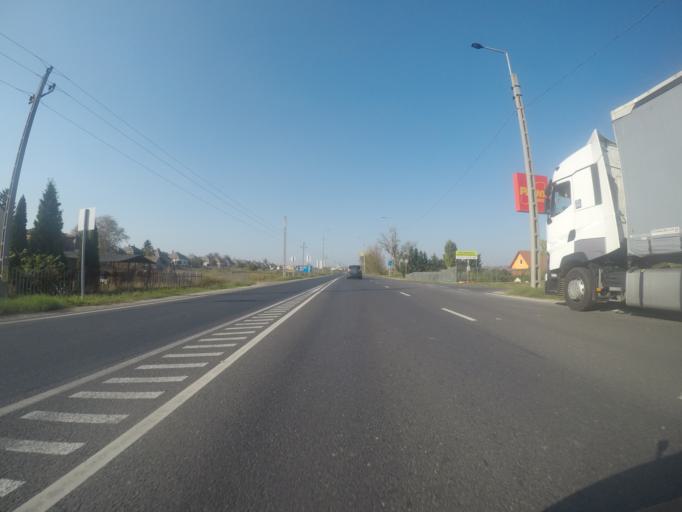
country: HU
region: Tolna
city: Dunafoldvar
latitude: 46.8033
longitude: 18.9167
